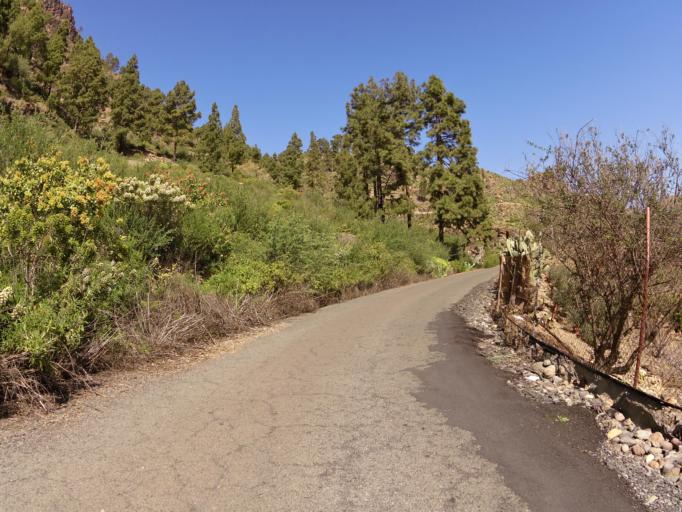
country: ES
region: Canary Islands
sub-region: Provincia de Las Palmas
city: Mogan
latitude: 27.8975
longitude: -15.6849
